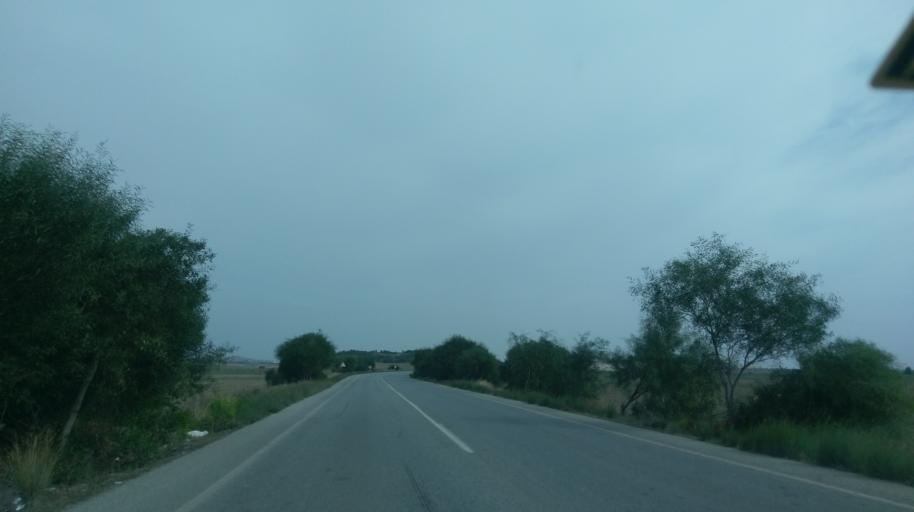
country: CY
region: Ammochostos
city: Trikomo
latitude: 35.2778
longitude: 33.8617
